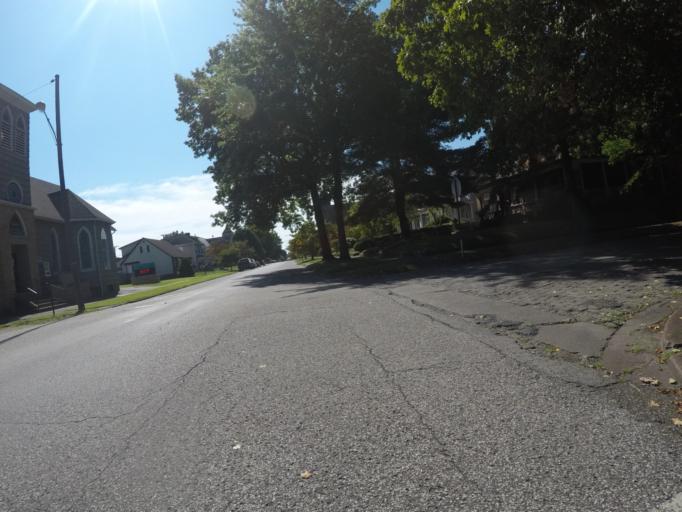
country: US
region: Ohio
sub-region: Lawrence County
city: Ironton
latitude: 38.5310
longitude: -82.6790
